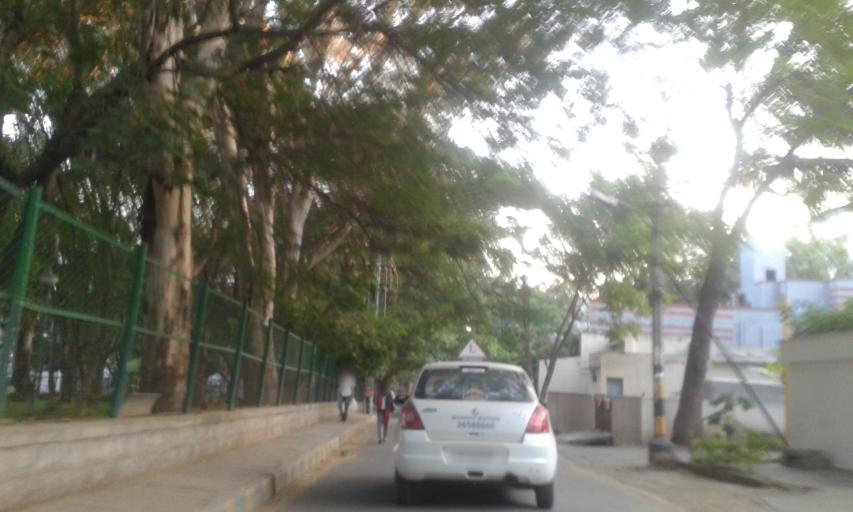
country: IN
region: Karnataka
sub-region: Bangalore Urban
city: Bangalore
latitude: 12.9083
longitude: 77.5990
